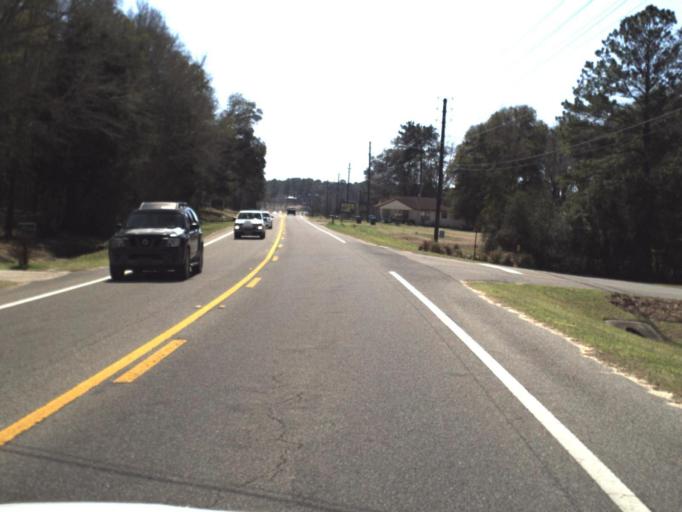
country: US
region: Florida
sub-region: Jackson County
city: Marianna
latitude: 30.7713
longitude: -85.2545
